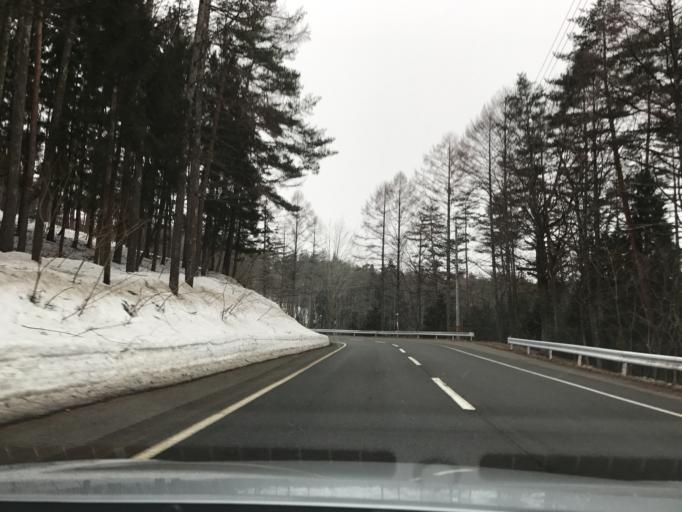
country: JP
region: Nagano
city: Omachi
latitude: 36.5634
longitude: 137.8677
